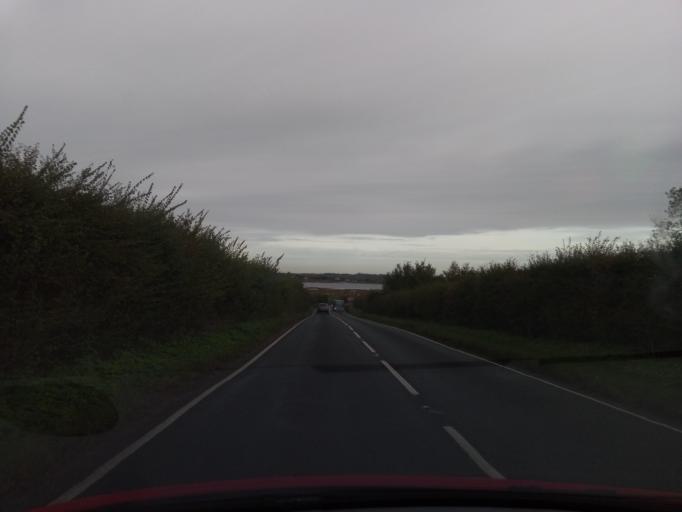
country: GB
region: England
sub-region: Essex
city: West Mersea
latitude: 51.7890
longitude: 0.9211
